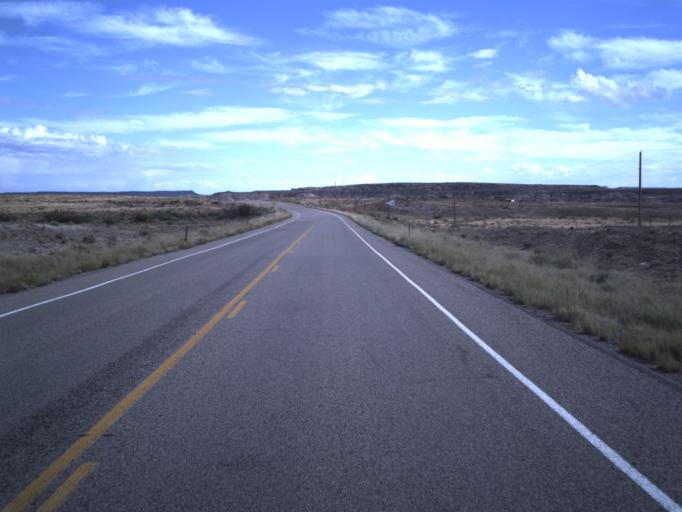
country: US
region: Colorado
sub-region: Montezuma County
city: Towaoc
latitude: 37.1638
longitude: -109.0721
